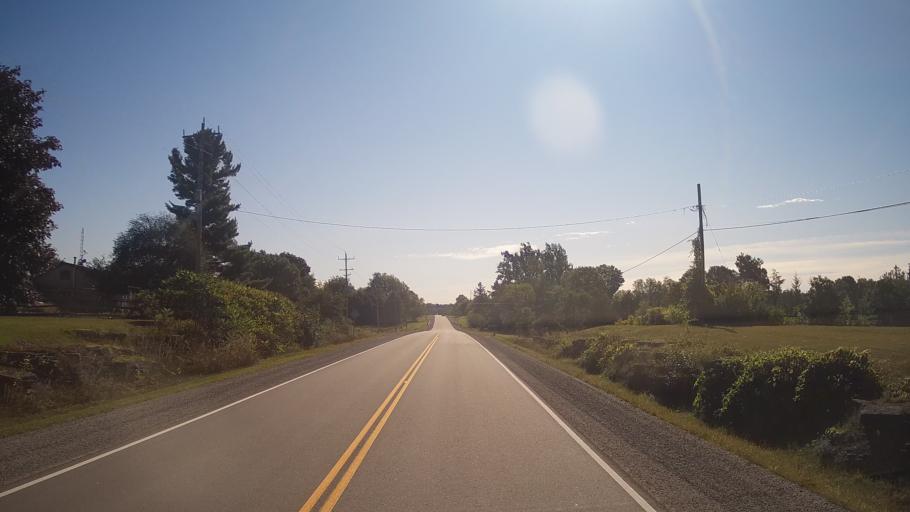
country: CA
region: Ontario
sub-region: Lanark County
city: Smiths Falls
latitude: 44.6268
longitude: -76.0090
